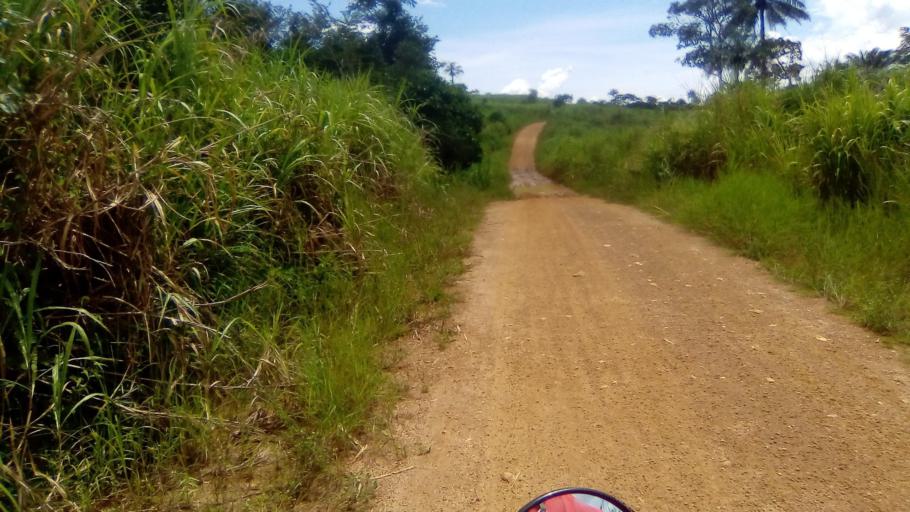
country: SL
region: Eastern Province
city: Simbakoro
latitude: 8.5439
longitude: -10.9357
